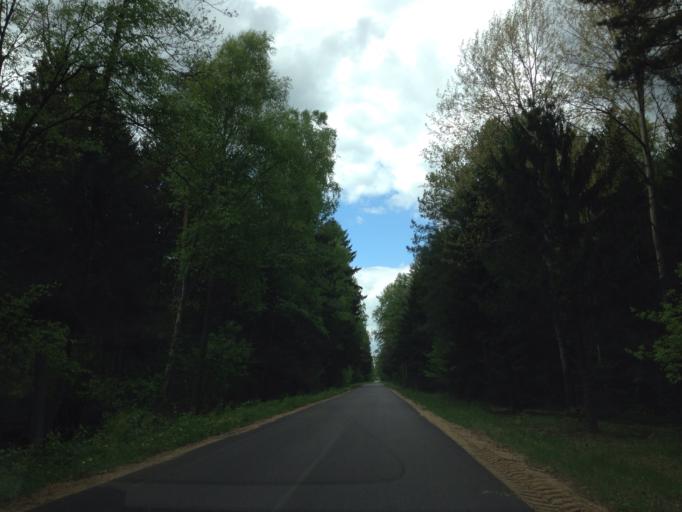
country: PL
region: Podlasie
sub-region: Powiat moniecki
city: Goniadz
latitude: 53.3625
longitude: 22.5988
